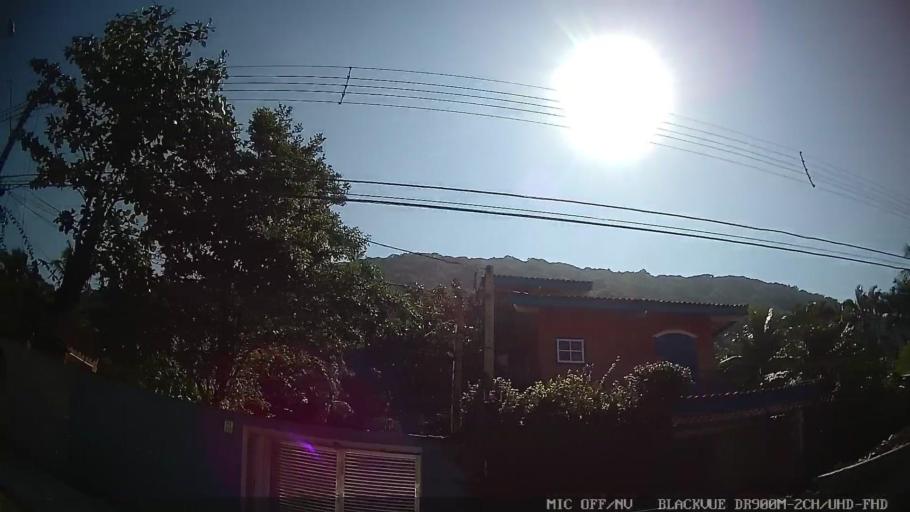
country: BR
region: Sao Paulo
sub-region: Guaruja
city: Guaruja
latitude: -24.0138
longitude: -46.2871
